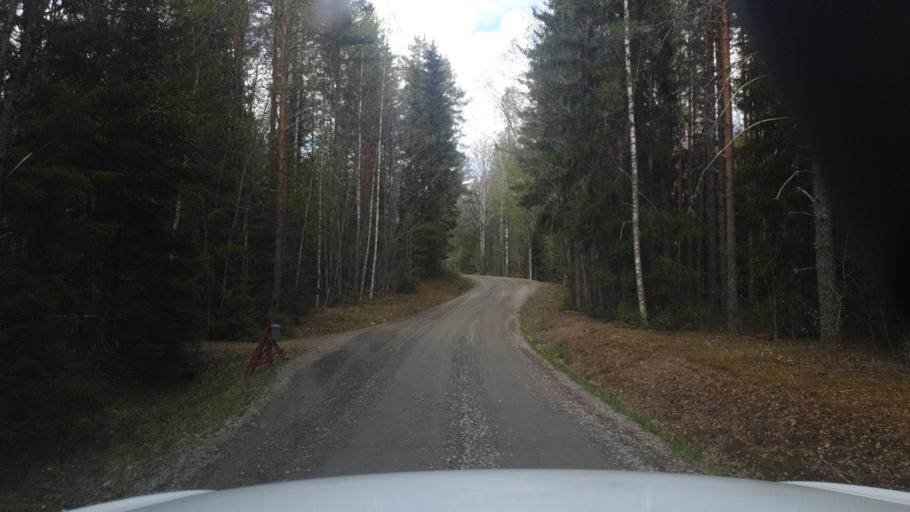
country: SE
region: Vaermland
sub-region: Sunne Kommun
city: Sunne
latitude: 59.6412
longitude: 13.0597
